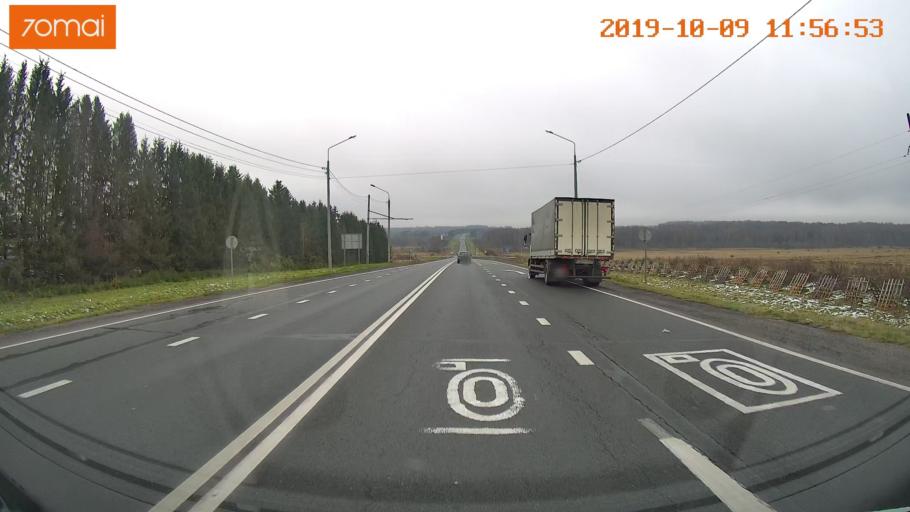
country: RU
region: Vologda
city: Gryazovets
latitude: 58.7390
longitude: 40.2897
